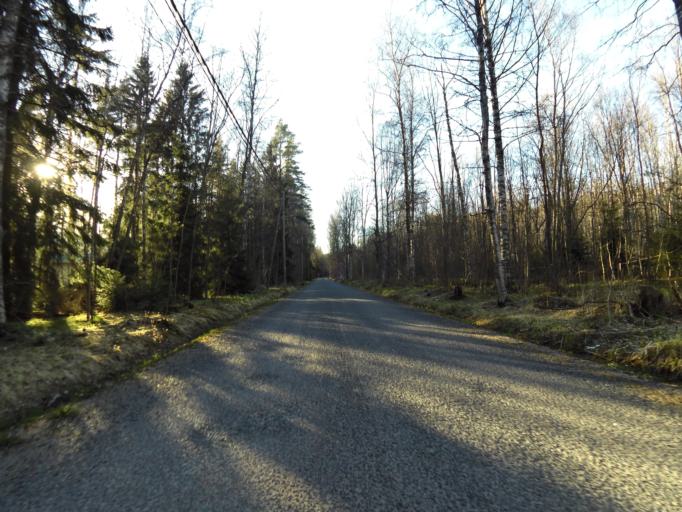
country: FI
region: Uusimaa
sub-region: Helsinki
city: Espoo
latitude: 60.1804
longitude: 24.6881
